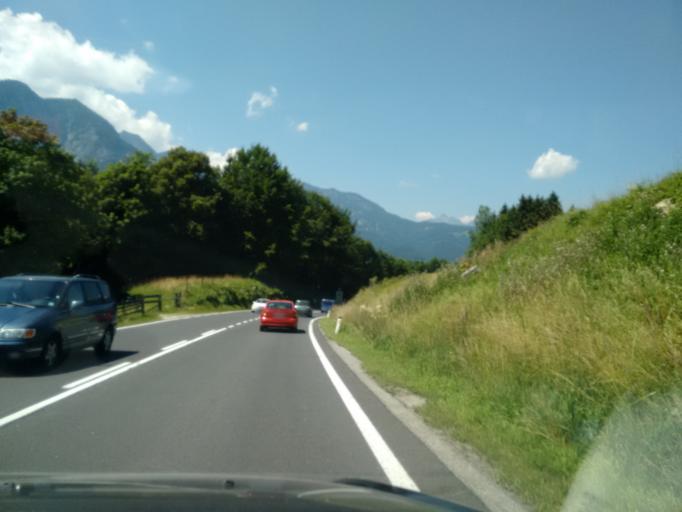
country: AT
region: Upper Austria
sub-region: Politischer Bezirk Gmunden
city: Bad Goisern
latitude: 47.6170
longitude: 13.6555
